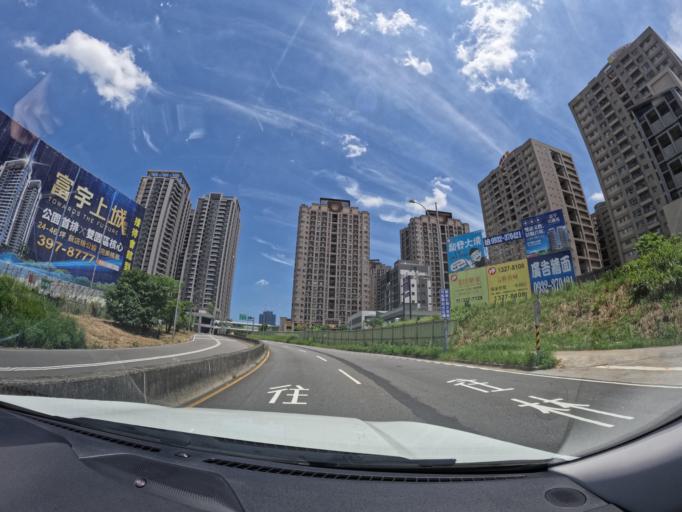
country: TW
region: Taipei
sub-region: Taipei
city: Banqiao
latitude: 25.0389
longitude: 121.3872
